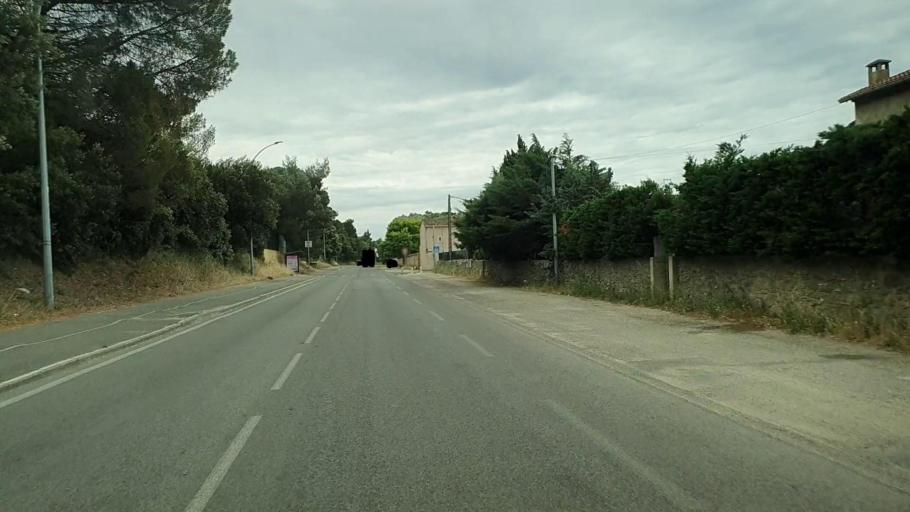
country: FR
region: Languedoc-Roussillon
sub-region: Departement du Gard
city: Bagnols-sur-Ceze
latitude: 44.1474
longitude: 4.6118
